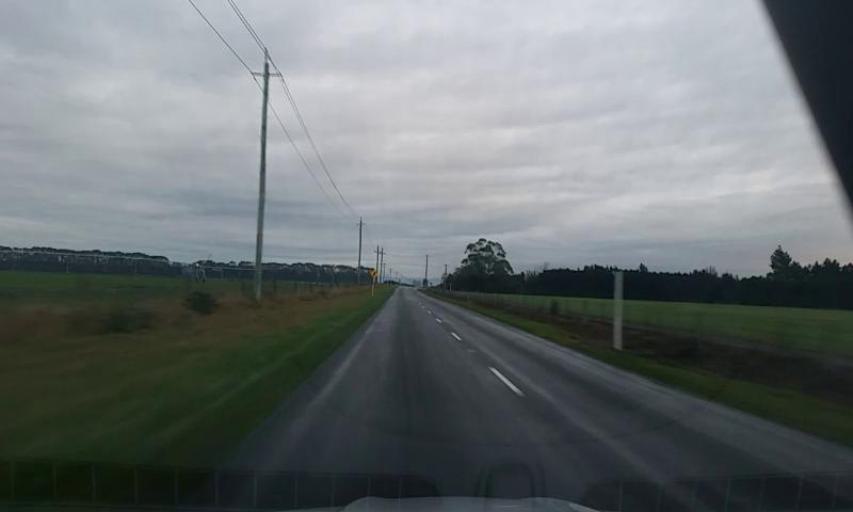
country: NZ
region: Canterbury
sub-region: Ashburton District
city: Rakaia
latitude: -43.7528
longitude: 171.8651
